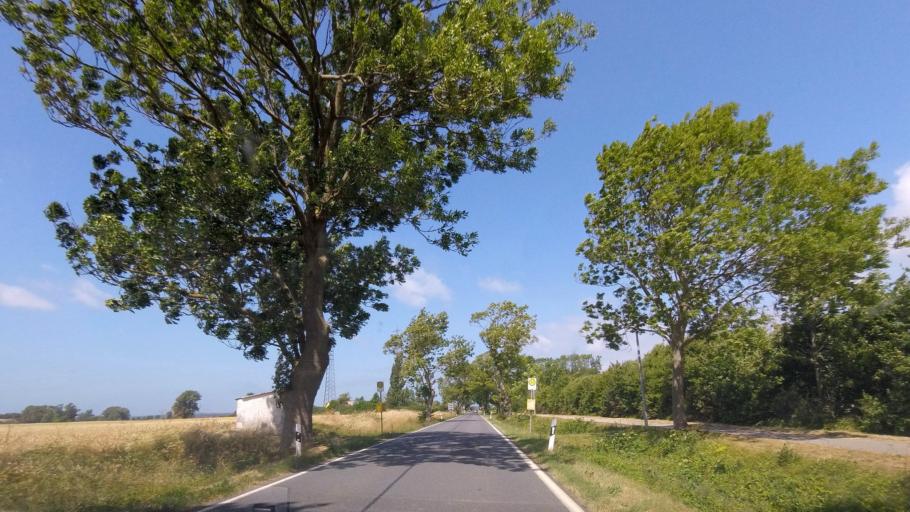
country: DE
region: Mecklenburg-Vorpommern
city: Wiek
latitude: 54.5491
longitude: 13.2459
